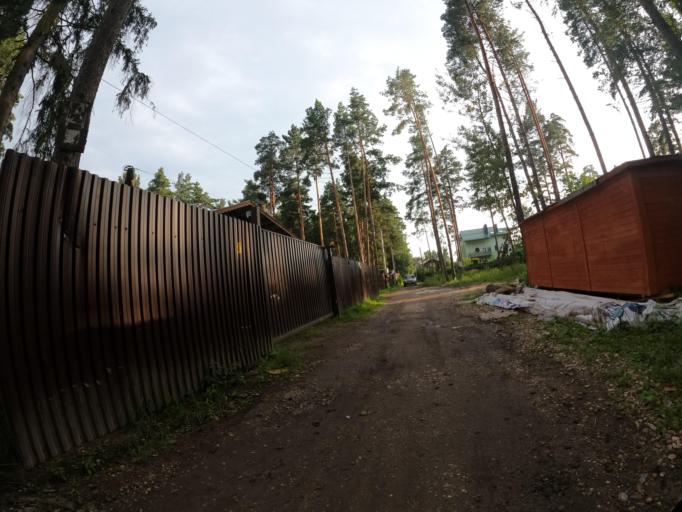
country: RU
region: Moskovskaya
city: Il'inskiy
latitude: 55.6349
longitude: 38.1128
